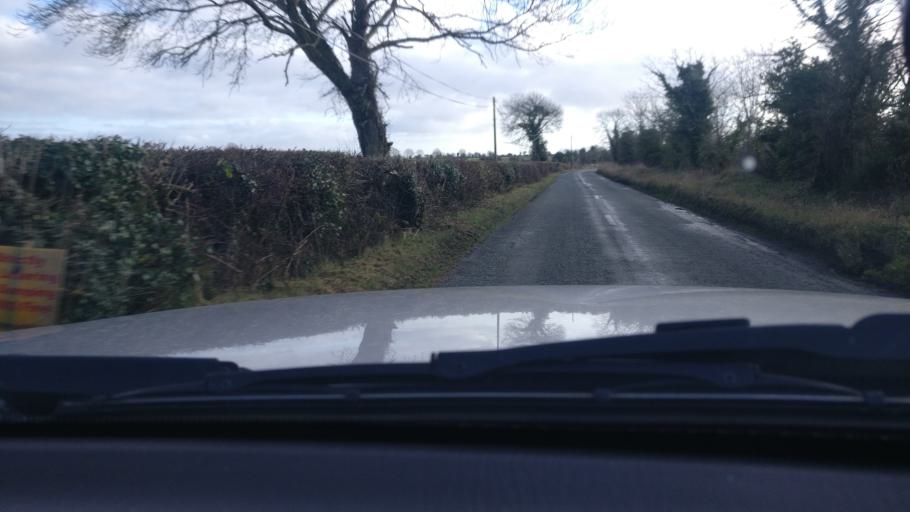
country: IE
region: Connaught
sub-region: County Galway
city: Ballinasloe
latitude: 53.2276
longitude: -8.2943
